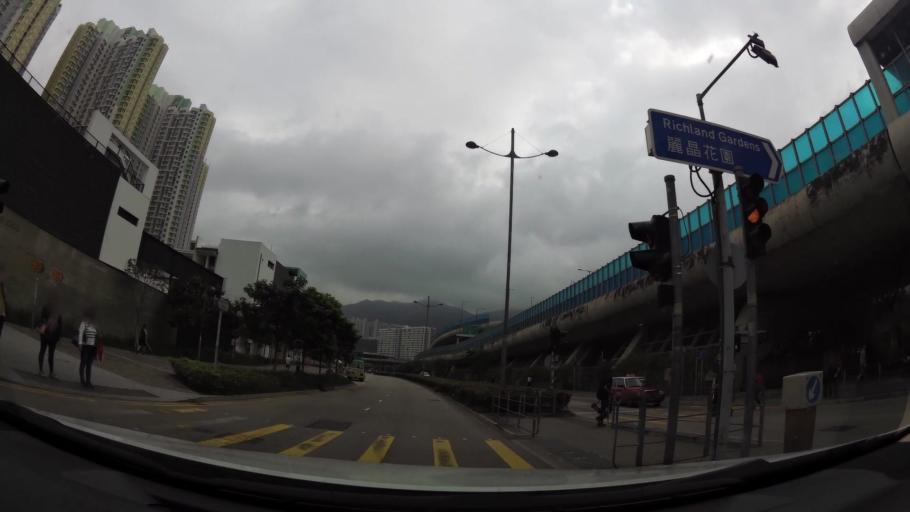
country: HK
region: Kowloon City
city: Kowloon
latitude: 22.3313
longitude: 114.2048
